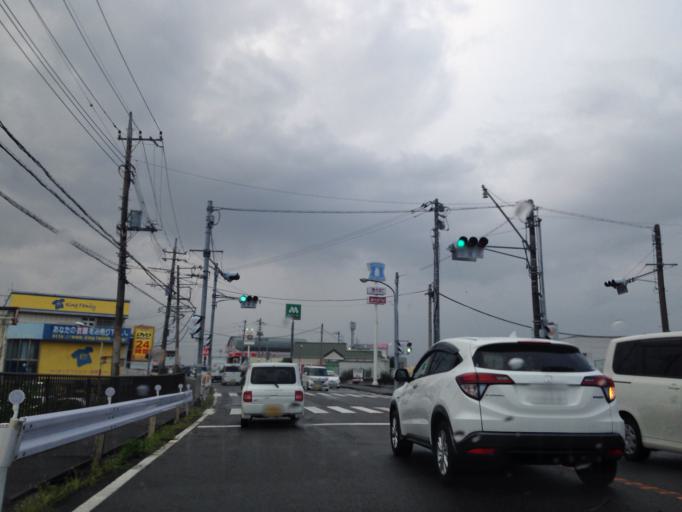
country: JP
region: Shizuoka
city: Mishima
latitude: 35.0721
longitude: 138.9415
